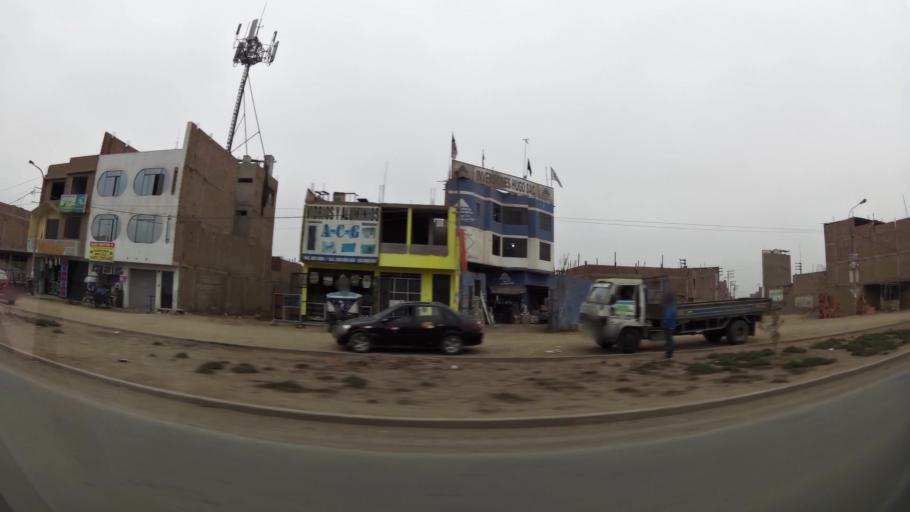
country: PE
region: Lima
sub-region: Lima
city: Urb. Santo Domingo
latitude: -11.8733
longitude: -77.0232
